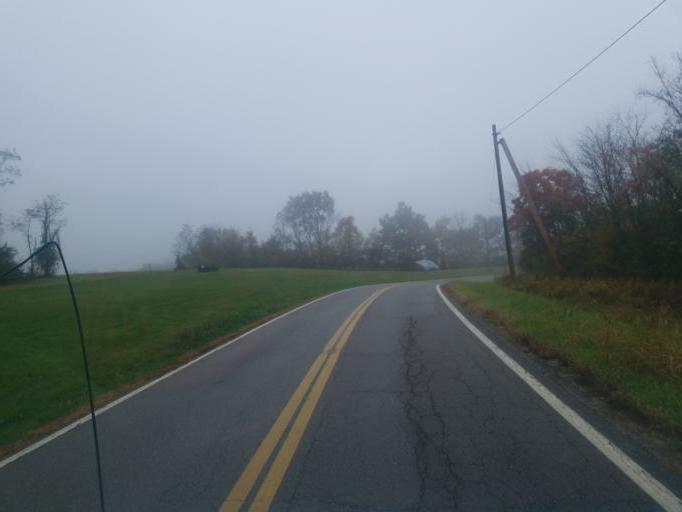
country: US
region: Ohio
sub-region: Morgan County
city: McConnelsville
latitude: 39.5352
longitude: -81.7999
